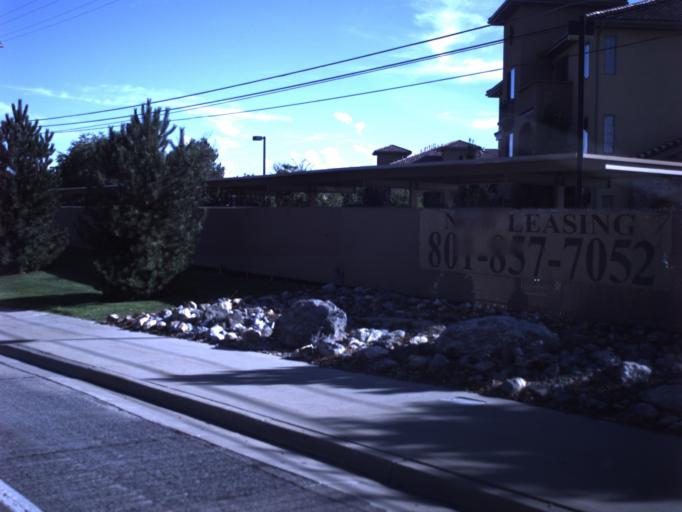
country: US
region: Utah
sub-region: Utah County
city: Orem
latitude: 40.2641
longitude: -111.6797
